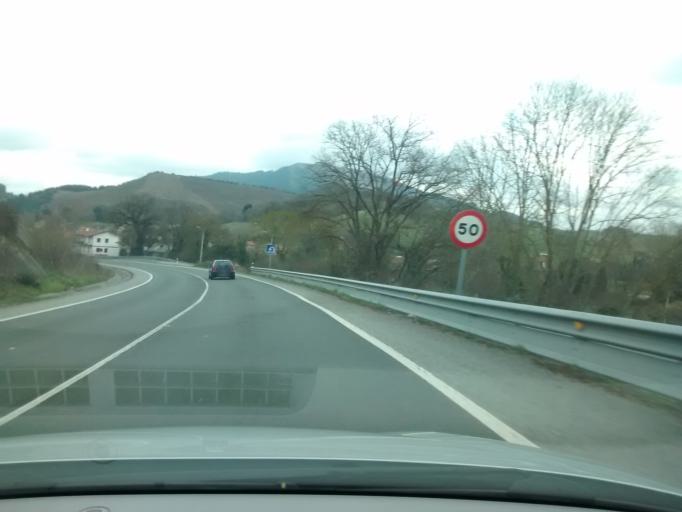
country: ES
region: Basque Country
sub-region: Bizkaia
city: Balmaseda
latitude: 43.1643
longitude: -3.2323
